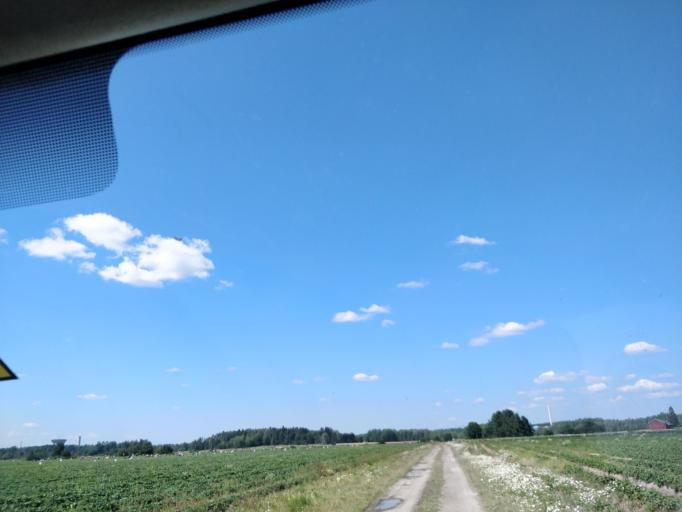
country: FI
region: Uusimaa
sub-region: Helsinki
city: Vantaa
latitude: 60.3066
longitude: 25.0751
